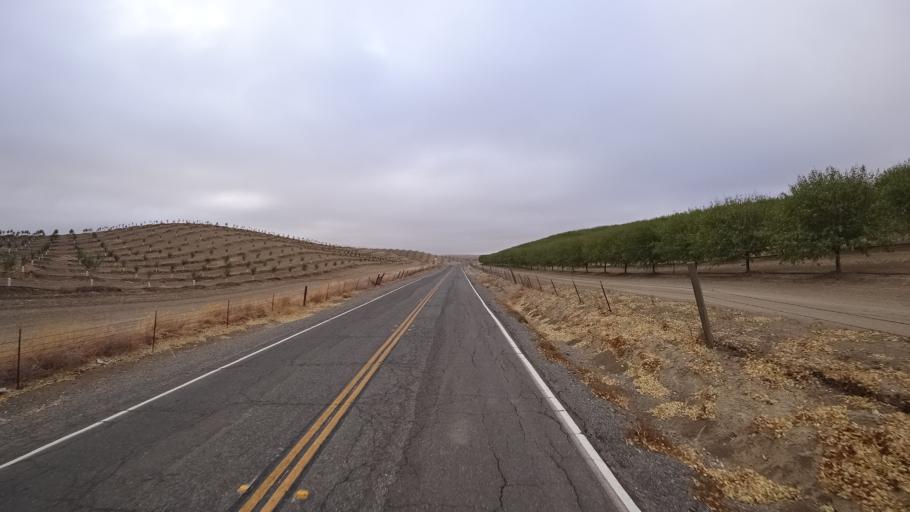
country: US
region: California
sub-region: Yolo County
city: Dunnigan
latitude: 38.8762
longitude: -122.0262
